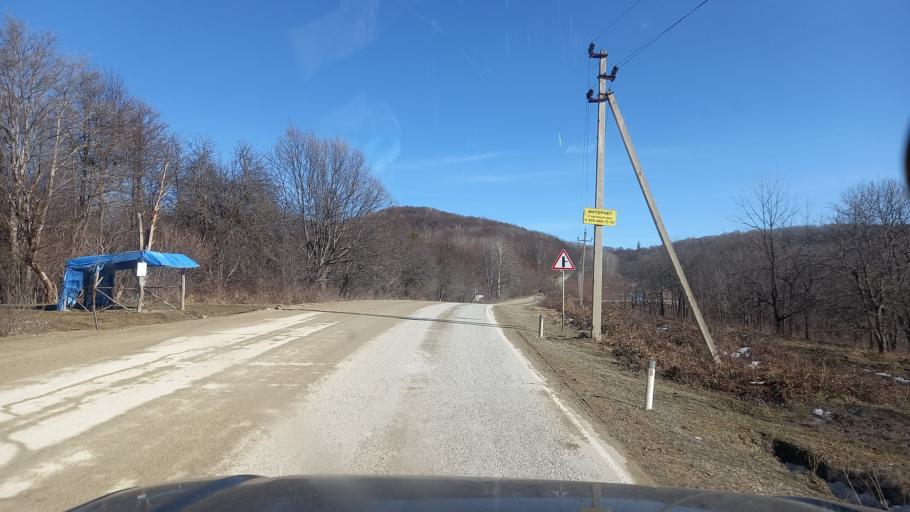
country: RU
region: Adygeya
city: Kamennomostskiy
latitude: 44.2864
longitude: 40.2983
